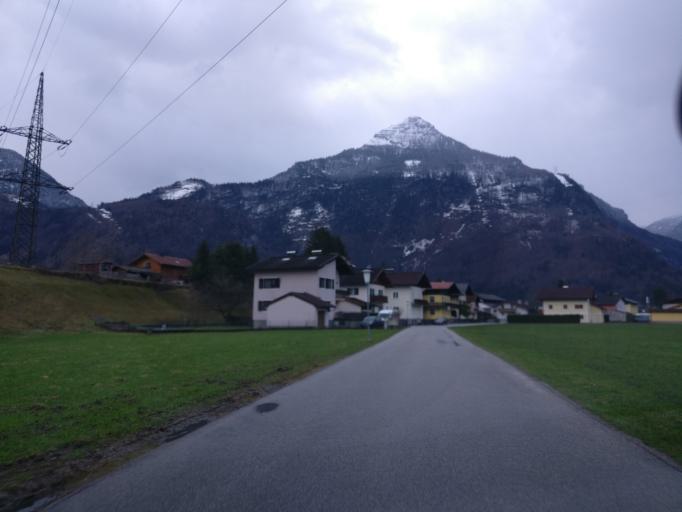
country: AT
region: Salzburg
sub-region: Politischer Bezirk Hallein
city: Golling an der Salzach
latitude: 47.5900
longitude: 13.1683
